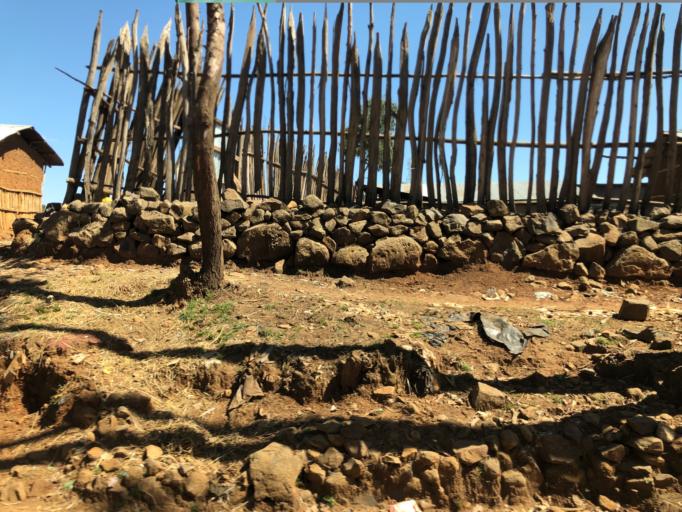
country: ET
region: Amhara
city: Lalibela
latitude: 11.6911
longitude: 38.9228
